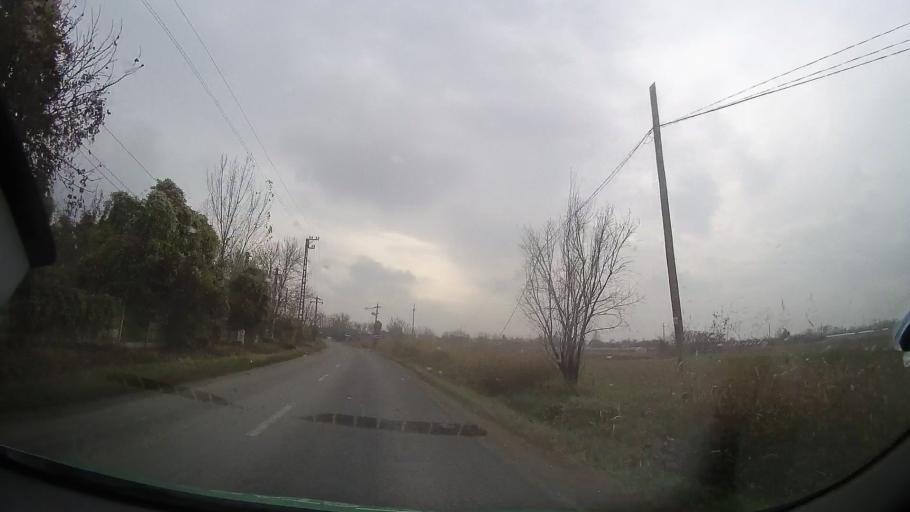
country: RO
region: Prahova
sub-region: Comuna Gherghita
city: Gherghita
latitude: 44.8031
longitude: 26.2669
